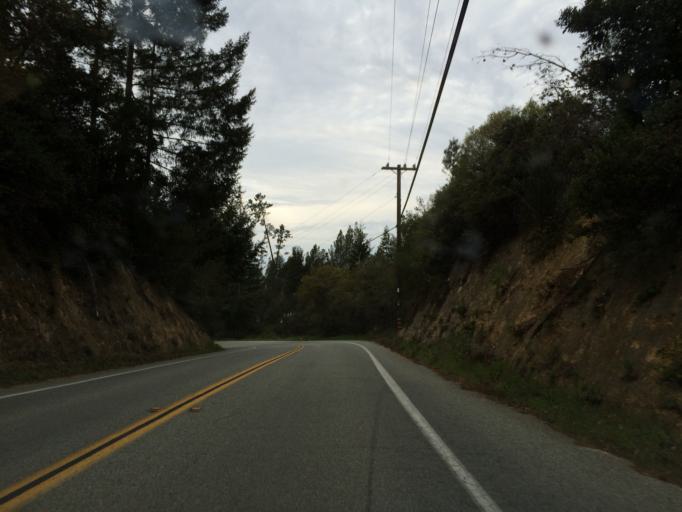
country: US
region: California
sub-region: Santa Cruz County
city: Felton
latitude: 37.0355
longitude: -122.1075
